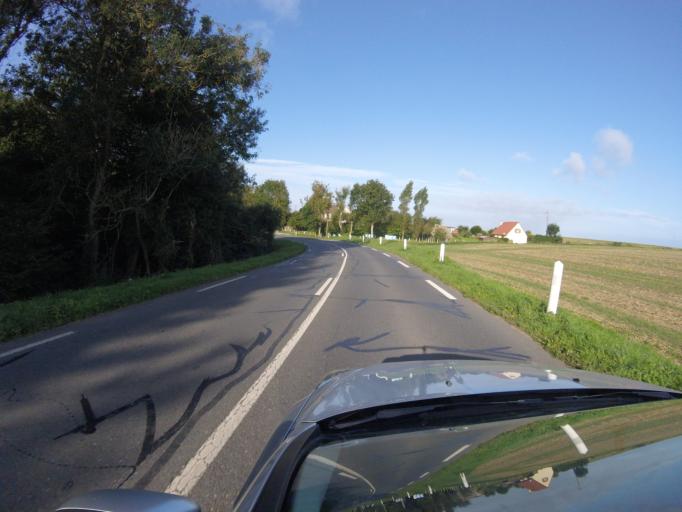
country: FR
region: Haute-Normandie
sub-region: Departement de la Seine-Maritime
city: Fecamp
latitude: 49.7683
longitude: 0.4068
